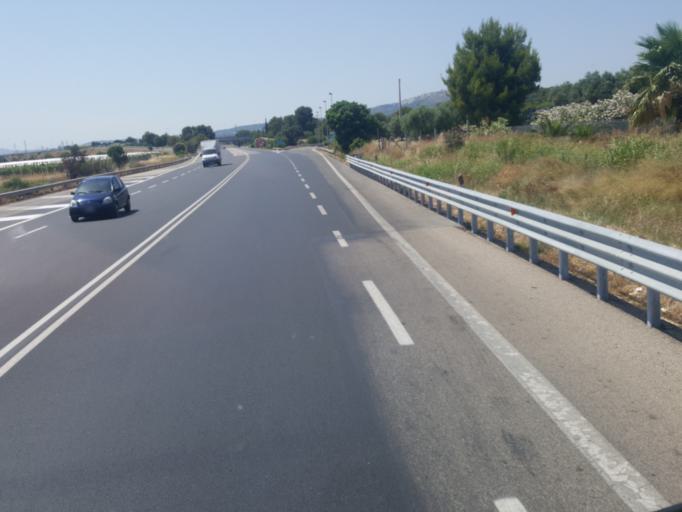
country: IT
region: Apulia
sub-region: Provincia di Taranto
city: Massafra
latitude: 40.5948
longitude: 17.0892
